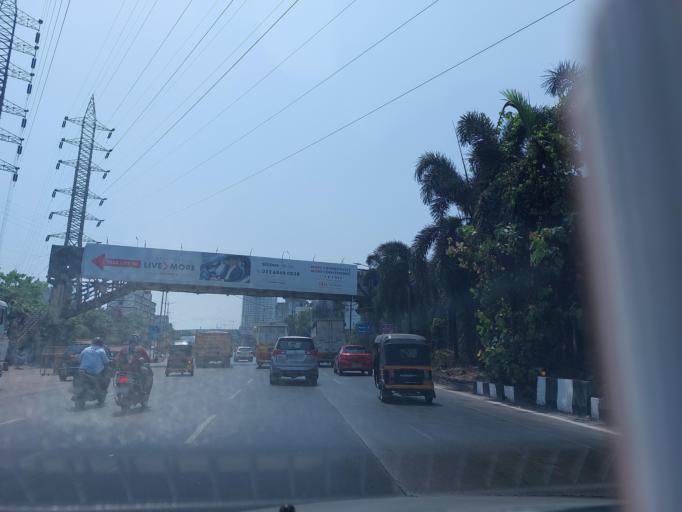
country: IN
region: Maharashtra
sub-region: Mumbai Suburban
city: Mumbai
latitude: 19.0529
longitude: 72.8811
